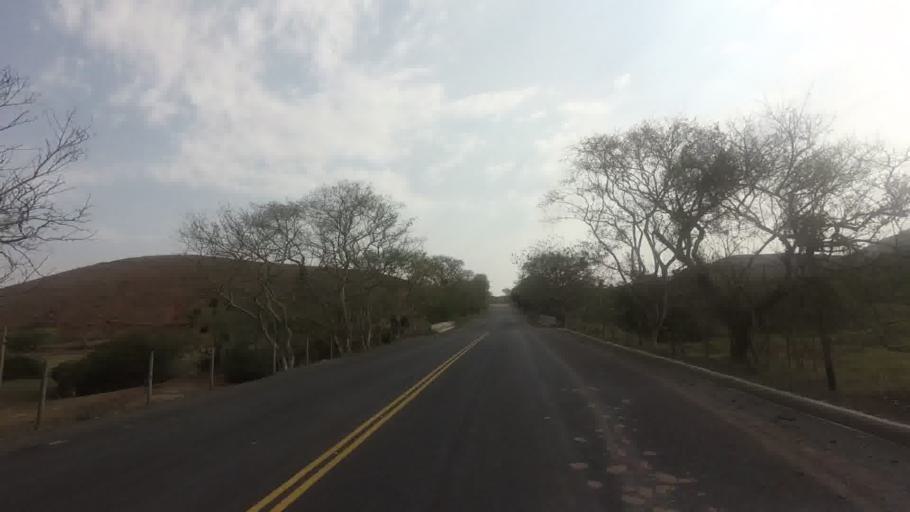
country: BR
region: Rio de Janeiro
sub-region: Itaperuna
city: Itaperuna
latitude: -21.2656
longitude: -41.7722
